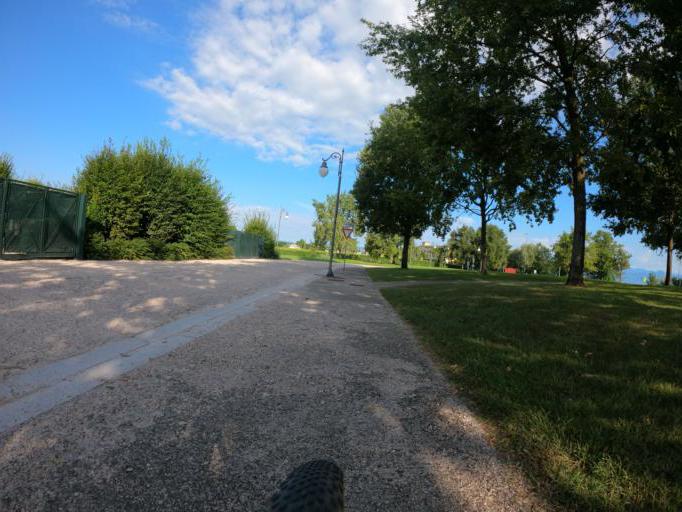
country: IT
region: Veneto
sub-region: Provincia di Verona
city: Peschiera del Garda
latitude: 45.4542
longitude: 10.6468
